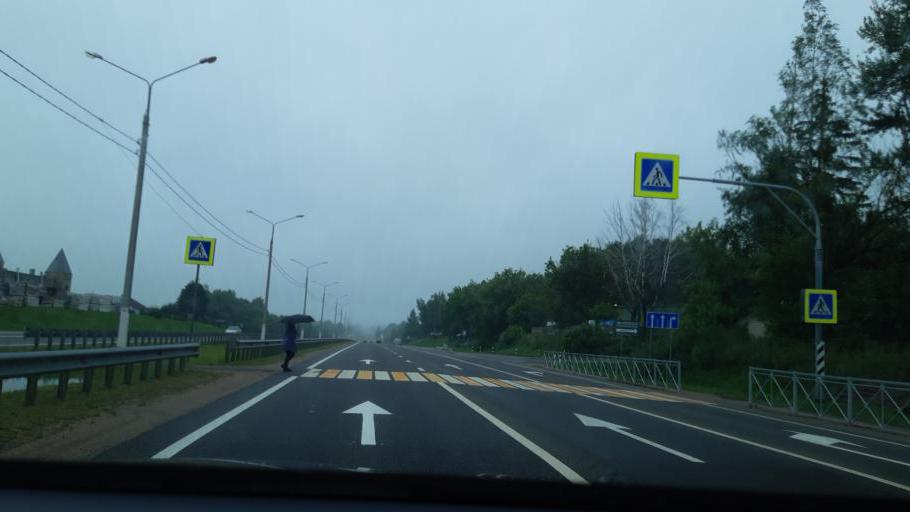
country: RU
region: Smolensk
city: Talashkino
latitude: 54.6494
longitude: 32.1692
